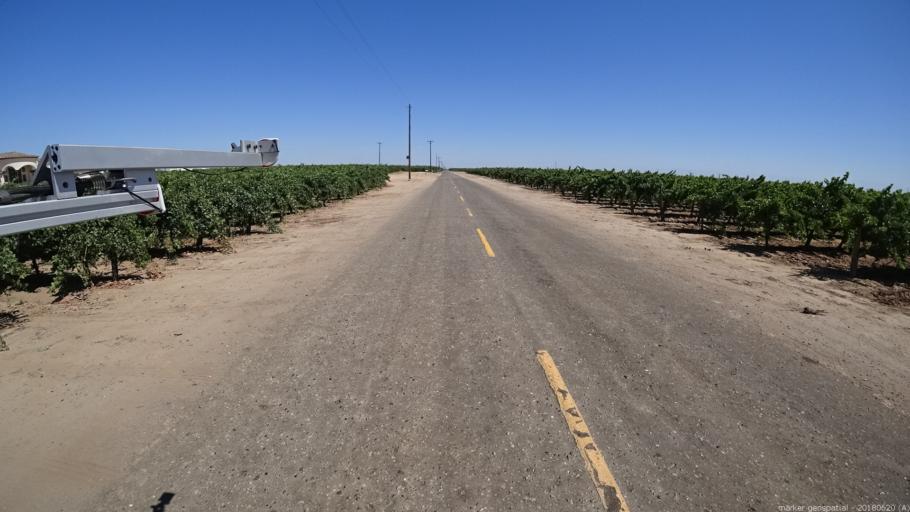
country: US
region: California
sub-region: Madera County
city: Parkwood
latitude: 36.8774
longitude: -120.0015
